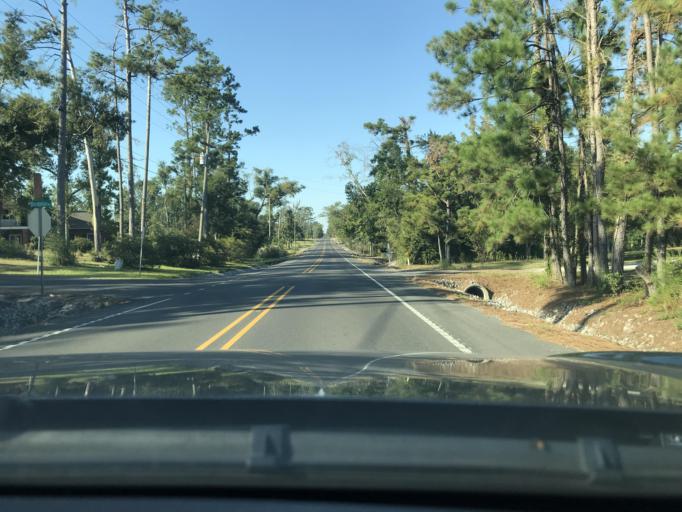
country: US
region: Louisiana
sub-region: Calcasieu Parish
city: Moss Bluff
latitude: 30.3338
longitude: -93.2580
